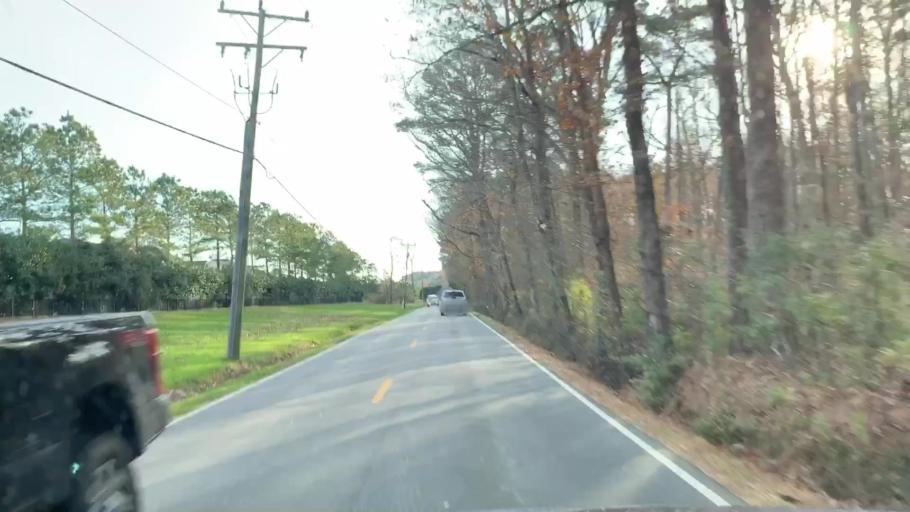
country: US
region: Virginia
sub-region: City of Virginia Beach
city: Virginia Beach
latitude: 36.7251
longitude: -76.0712
